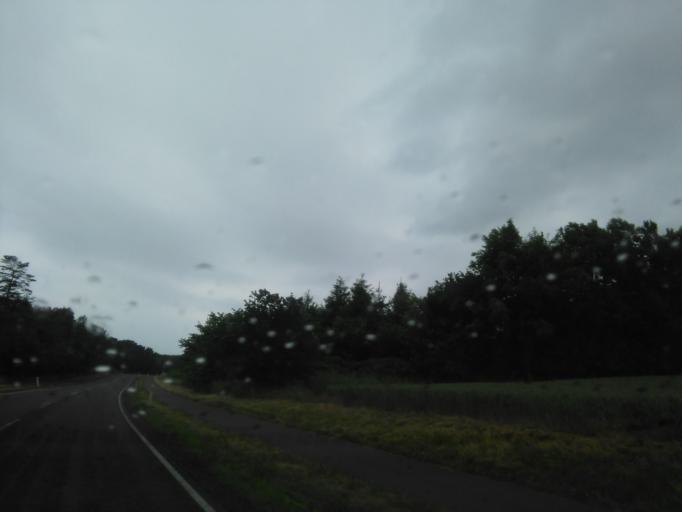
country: DK
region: Capital Region
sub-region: Bornholm Kommune
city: Akirkeby
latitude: 55.0509
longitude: 14.8103
